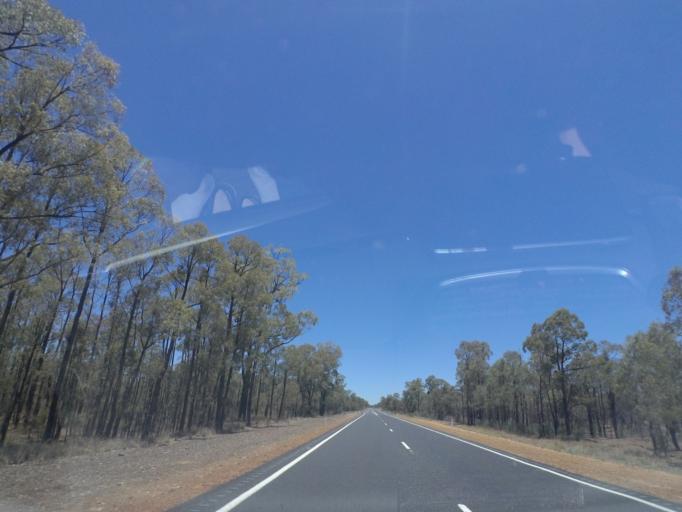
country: AU
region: New South Wales
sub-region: Warrumbungle Shire
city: Coonabarabran
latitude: -30.8654
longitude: 149.4523
